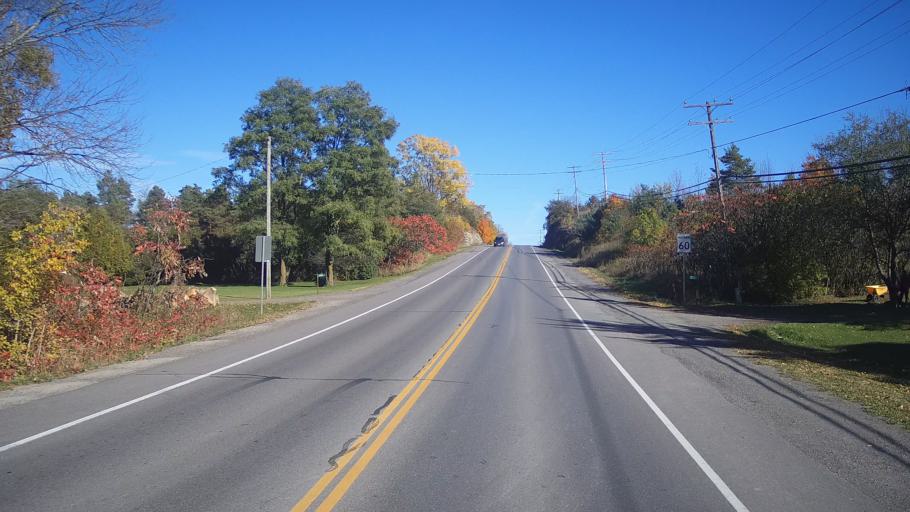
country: CA
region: Ontario
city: Kingston
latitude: 44.4071
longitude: -76.5881
